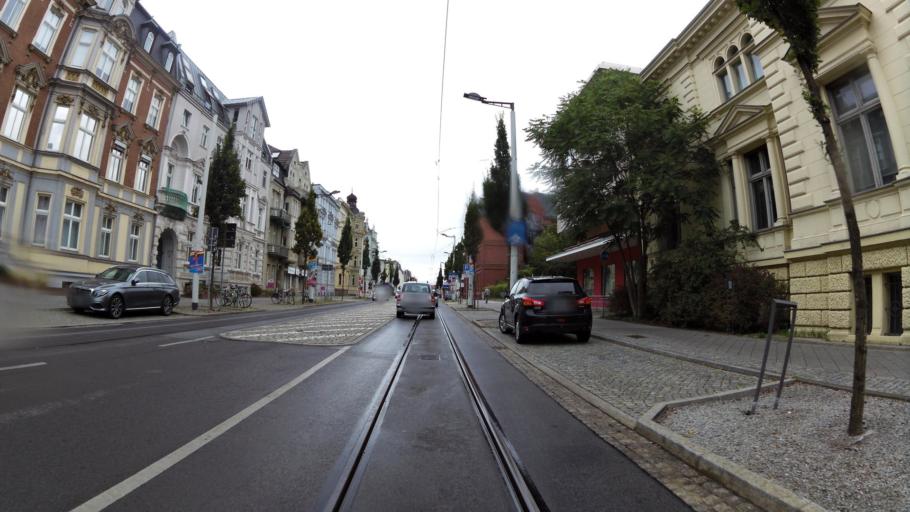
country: DE
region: Brandenburg
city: Cottbus
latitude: 51.7575
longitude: 14.3280
